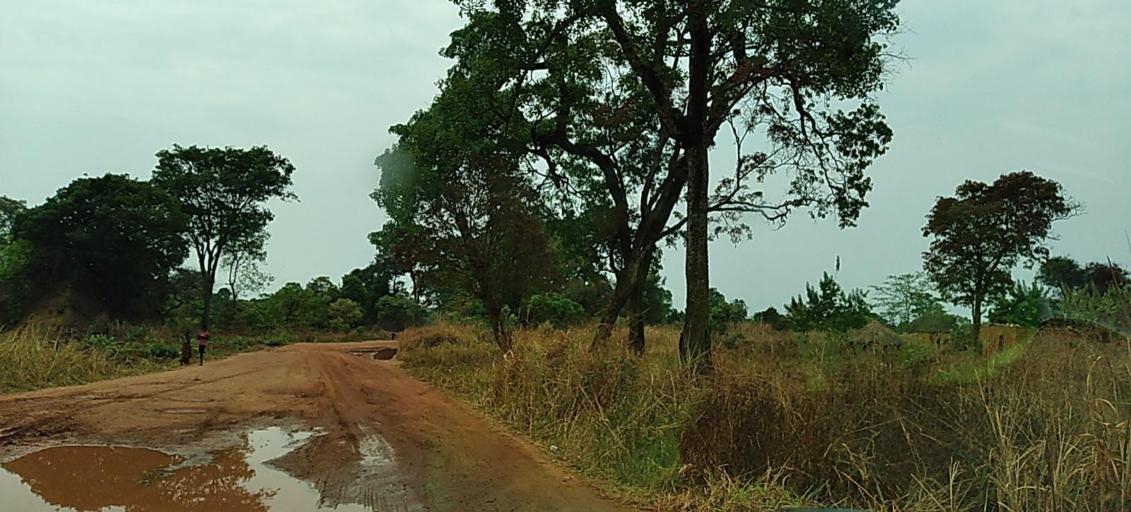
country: ZM
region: North-Western
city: Solwezi
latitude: -12.3427
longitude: 26.5271
